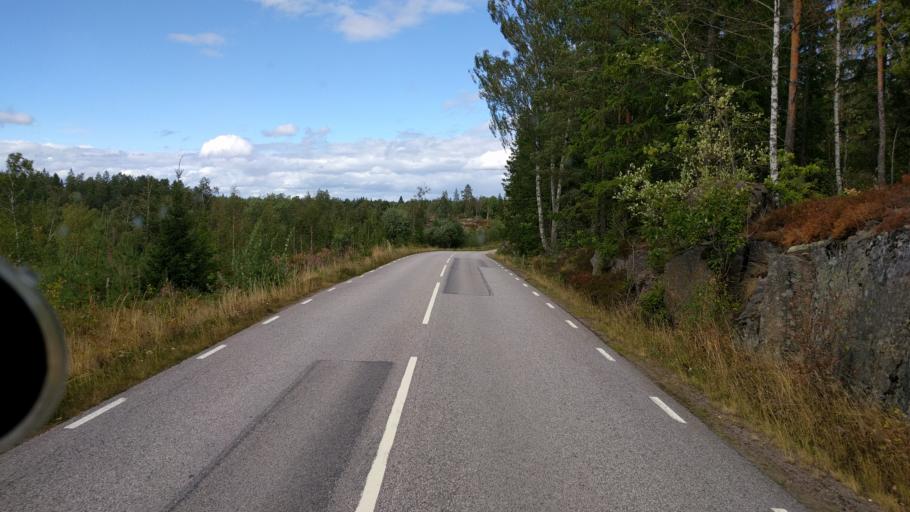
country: SE
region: Kalmar
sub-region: Vasterviks Kommun
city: Ankarsrum
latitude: 57.7417
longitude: 16.1090
